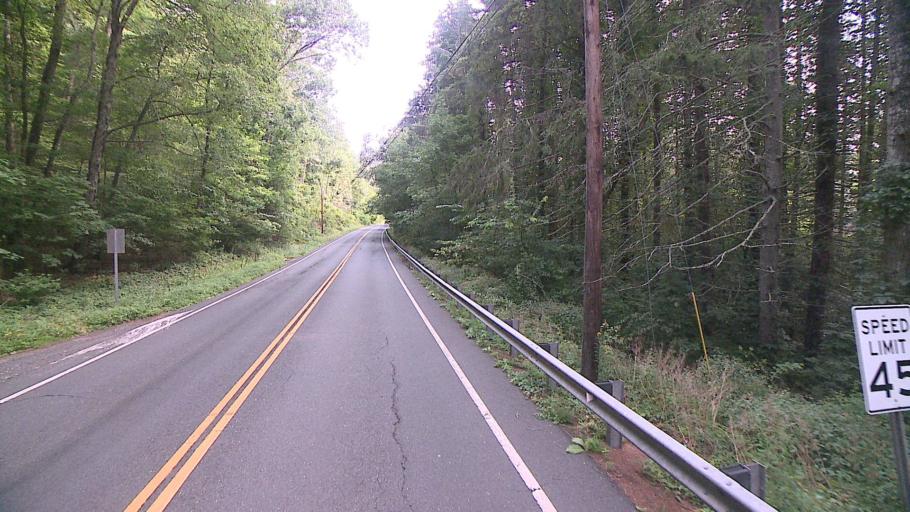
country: US
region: Connecticut
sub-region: Litchfield County
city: Canaan
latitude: 41.9233
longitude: -73.3636
